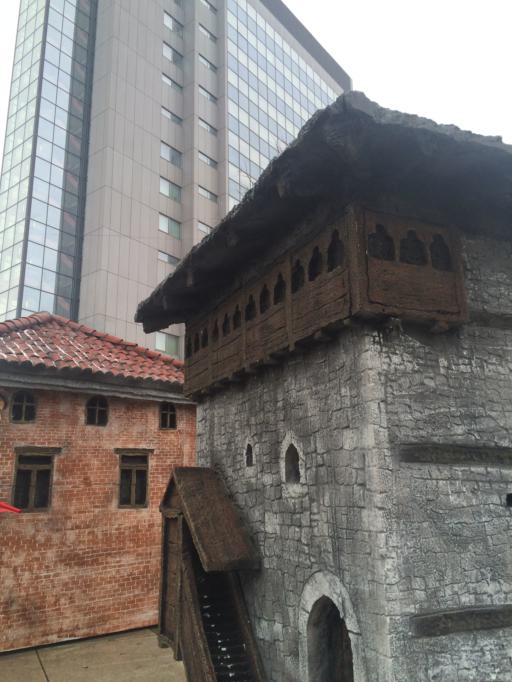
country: XK
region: Pristina
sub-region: Komuna e Prishtines
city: Pristina
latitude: 42.6639
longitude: 21.1640
